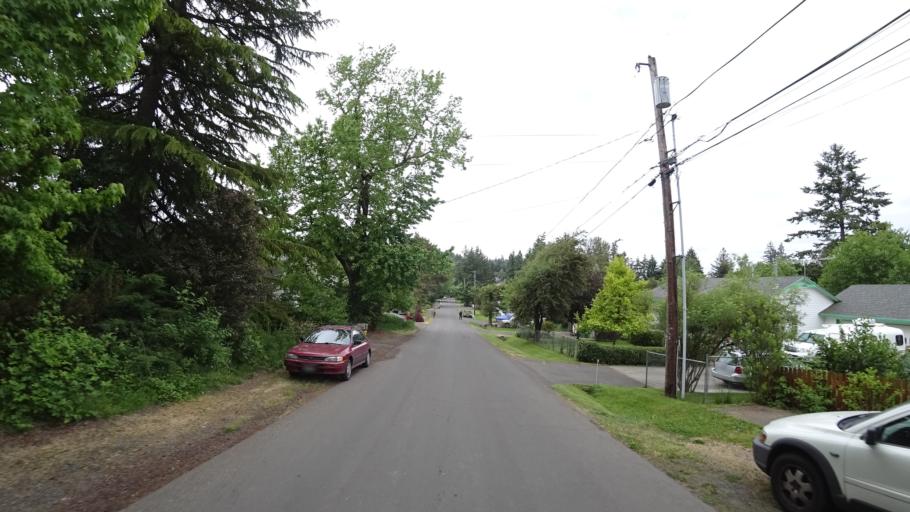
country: US
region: Oregon
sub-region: Washington County
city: Garden Home-Whitford
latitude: 45.4643
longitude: -122.7443
